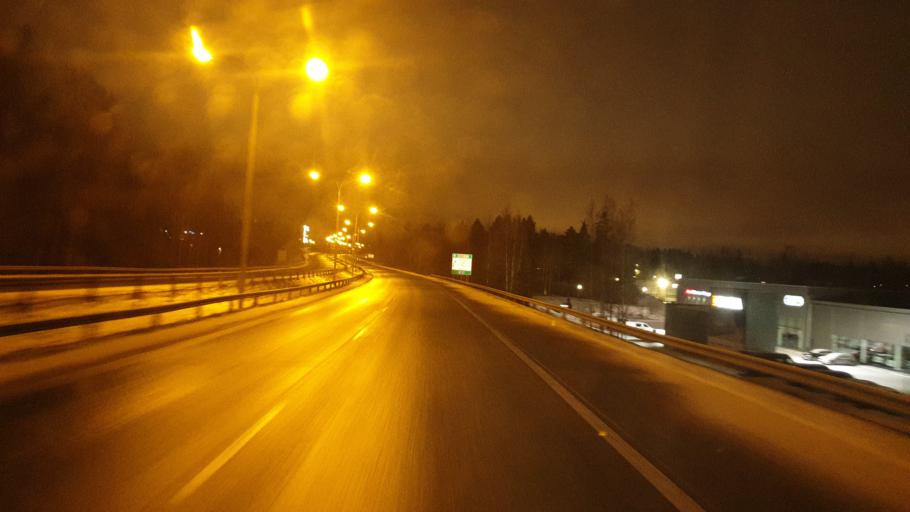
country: FI
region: Northern Savo
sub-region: Kuopio
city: Kuopio
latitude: 62.8541
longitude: 27.6205
